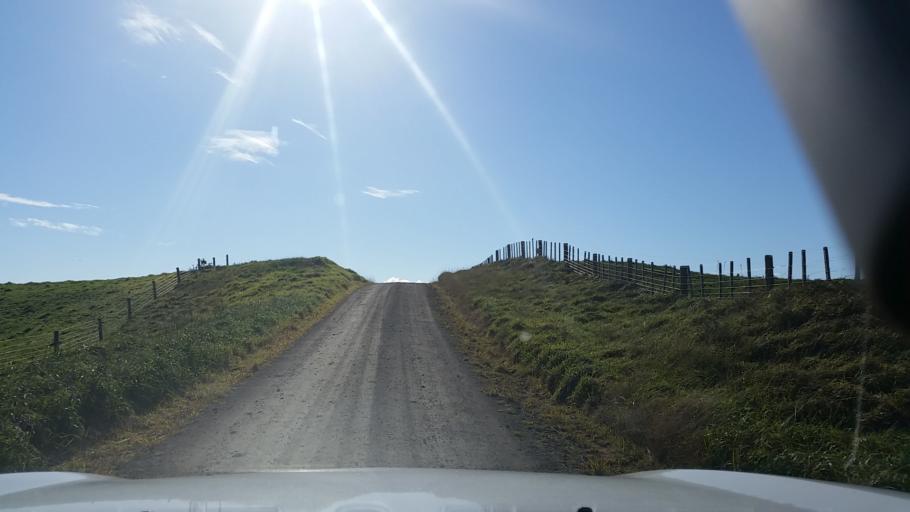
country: NZ
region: Taranaki
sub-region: South Taranaki District
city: Patea
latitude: -39.7794
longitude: 174.5474
